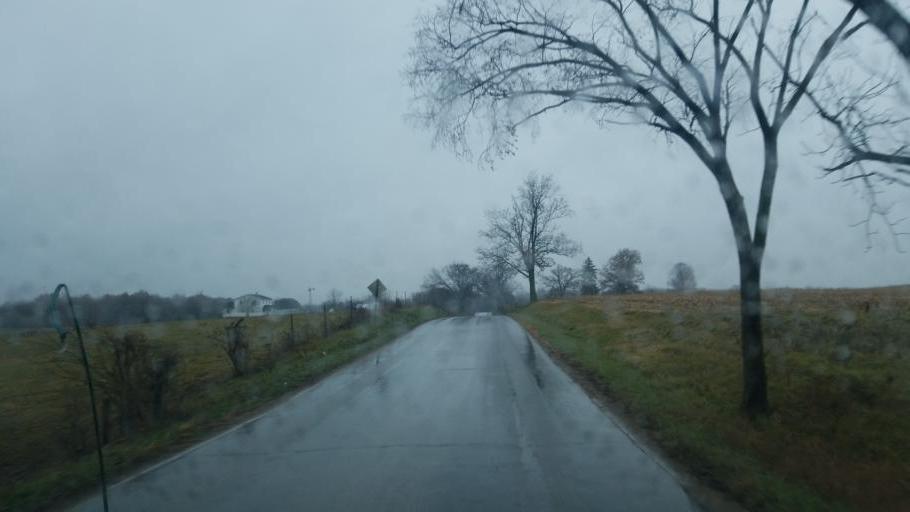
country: US
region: Indiana
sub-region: Adams County
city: Geneva
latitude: 40.6147
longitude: -84.9280
